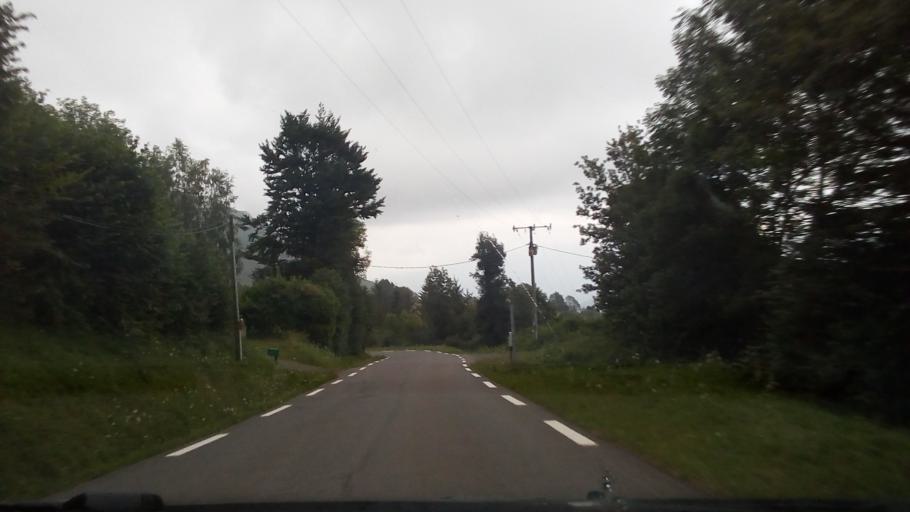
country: FR
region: Midi-Pyrenees
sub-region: Departement des Hautes-Pyrenees
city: Argeles-Gazost
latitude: 42.9652
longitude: -0.2288
